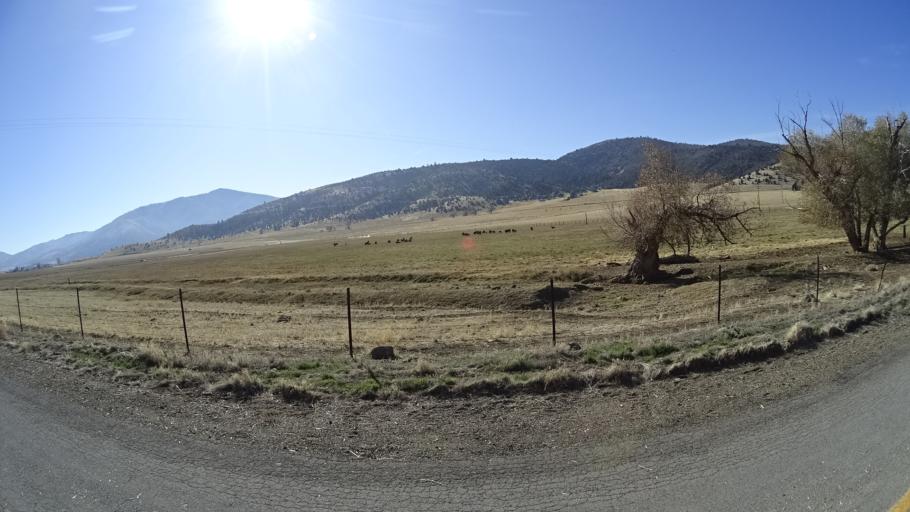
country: US
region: California
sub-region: Siskiyou County
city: Weed
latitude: 41.5277
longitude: -122.5332
